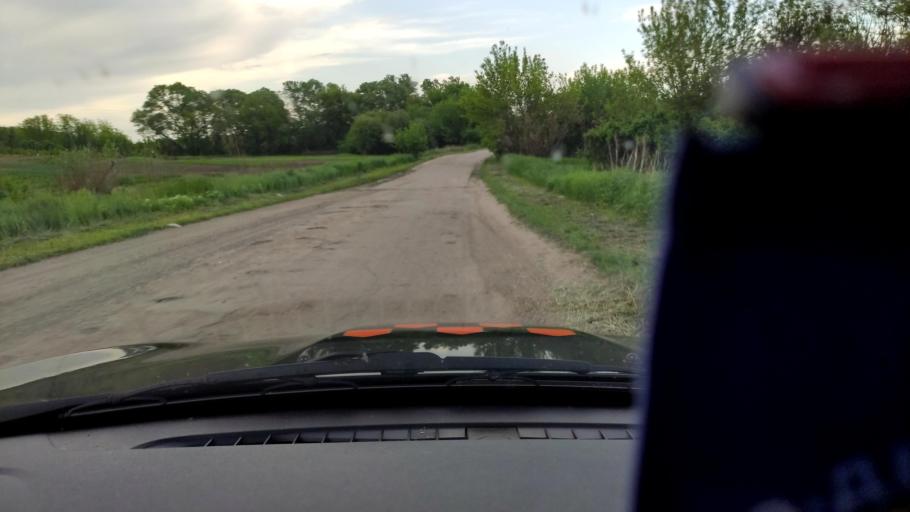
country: RU
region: Voronezj
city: Uryv-Pokrovka
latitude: 51.1146
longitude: 39.1610
